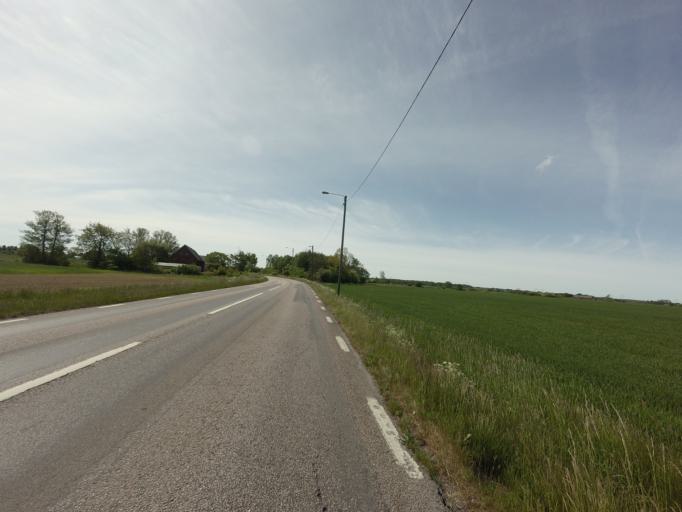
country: SE
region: Skane
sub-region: Helsingborg
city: Odakra
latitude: 56.1497
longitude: 12.6782
